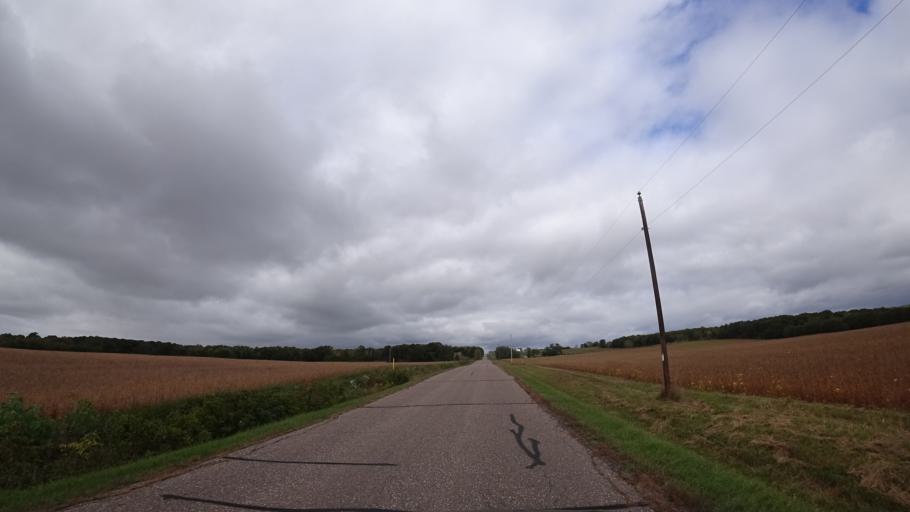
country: US
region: Wisconsin
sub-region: Chippewa County
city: Lake Wissota
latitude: 44.9837
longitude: -91.2868
